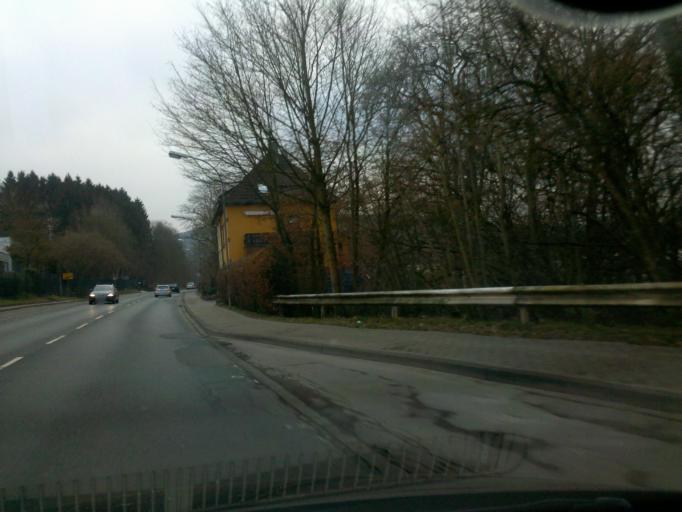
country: DE
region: North Rhine-Westphalia
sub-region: Regierungsbezirk Arnsberg
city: Olpe
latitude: 51.0154
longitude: 7.8395
